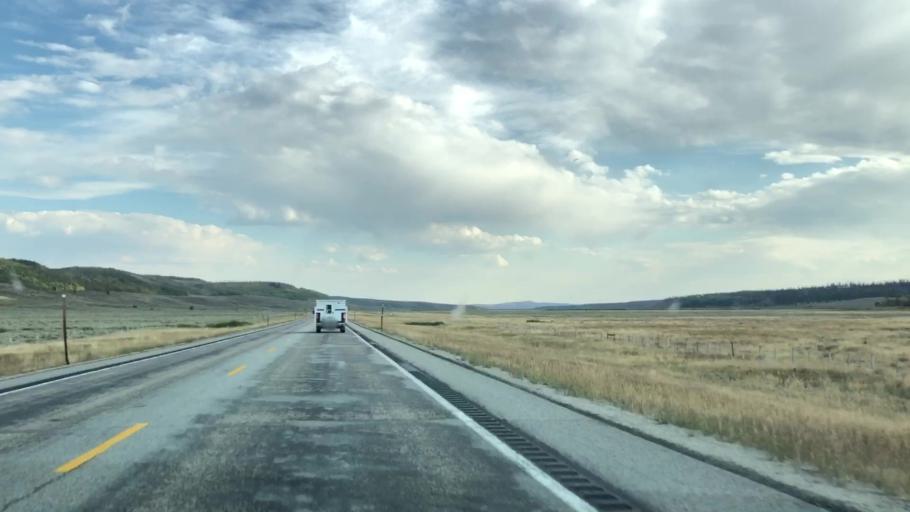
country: US
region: Wyoming
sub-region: Sublette County
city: Pinedale
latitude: 43.1089
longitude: -110.1728
